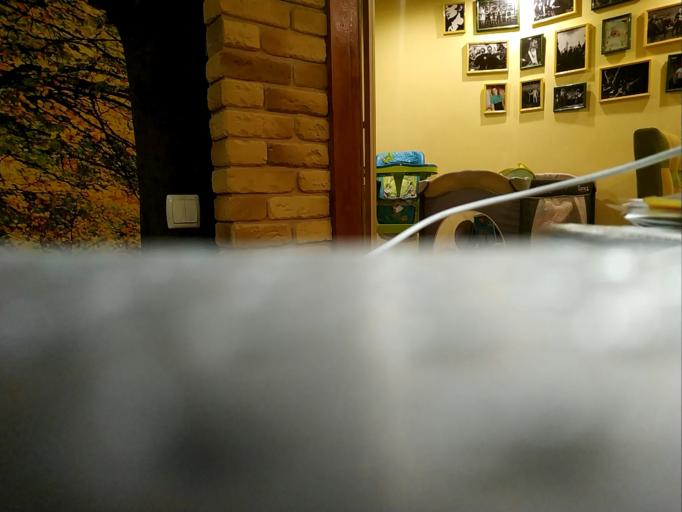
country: RU
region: Tverskaya
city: Spirovo
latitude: 57.3479
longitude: 35.0383
